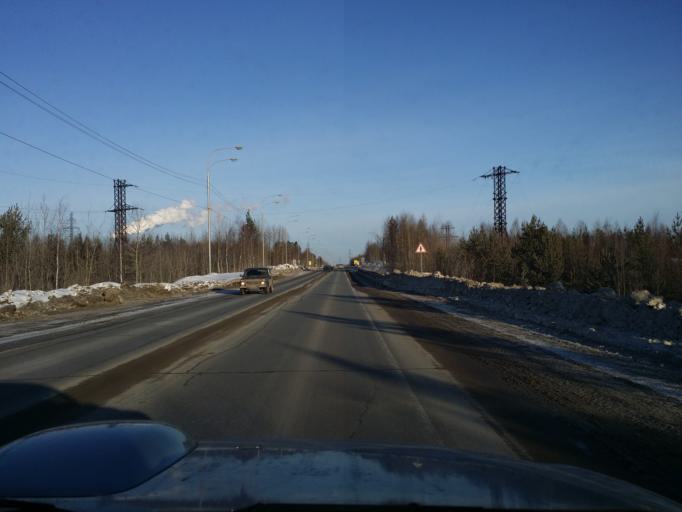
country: RU
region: Khanty-Mansiyskiy Avtonomnyy Okrug
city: Izluchinsk
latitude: 60.9650
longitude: 76.8549
